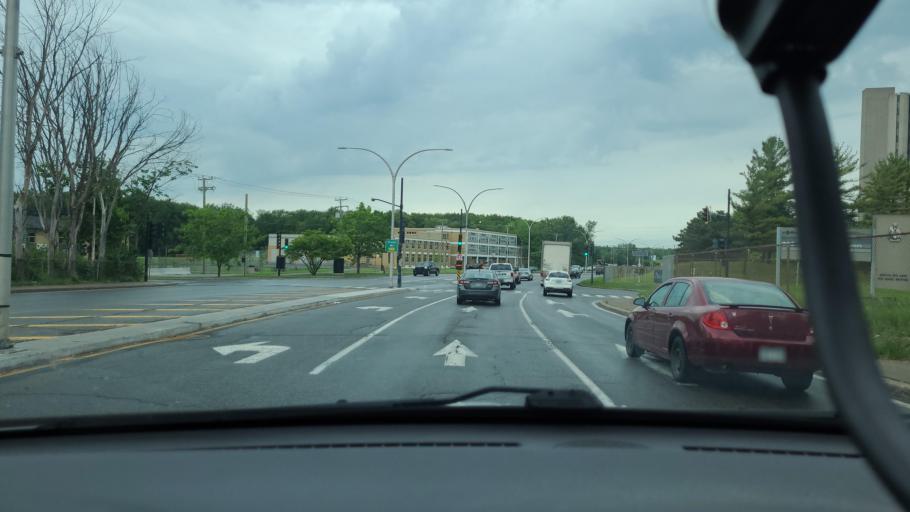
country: CA
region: Quebec
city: Sainte-Anne-de-Bellevue
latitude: 45.4109
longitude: -73.9511
